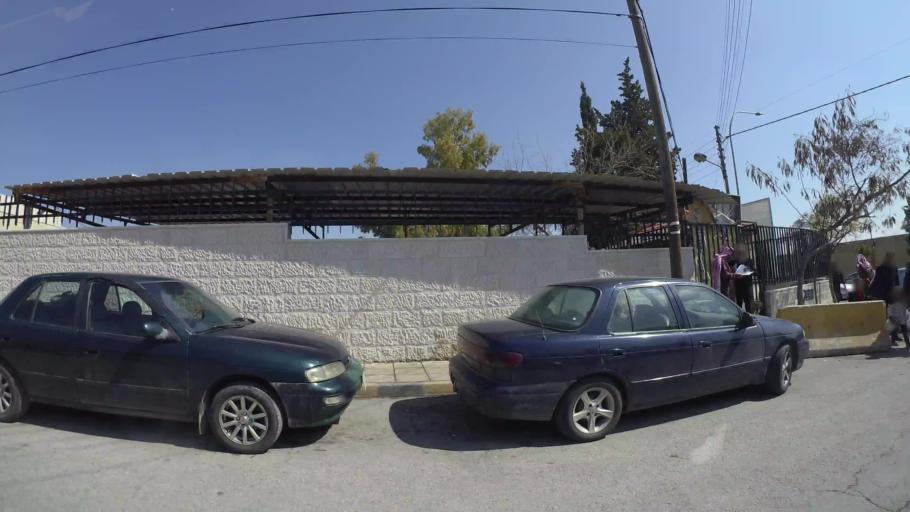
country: JO
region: Amman
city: Amman
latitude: 31.9750
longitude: 35.9756
